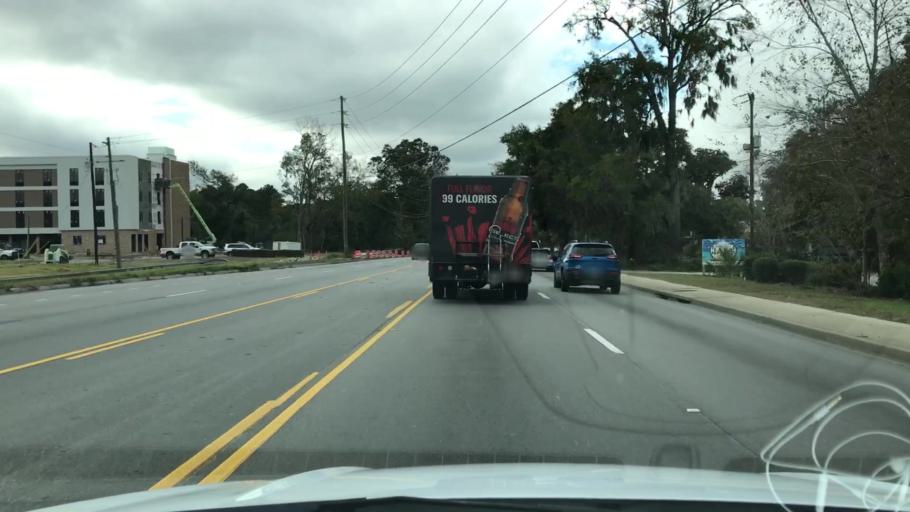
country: US
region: South Carolina
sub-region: Beaufort County
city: Burton
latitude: 32.4423
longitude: -80.7232
